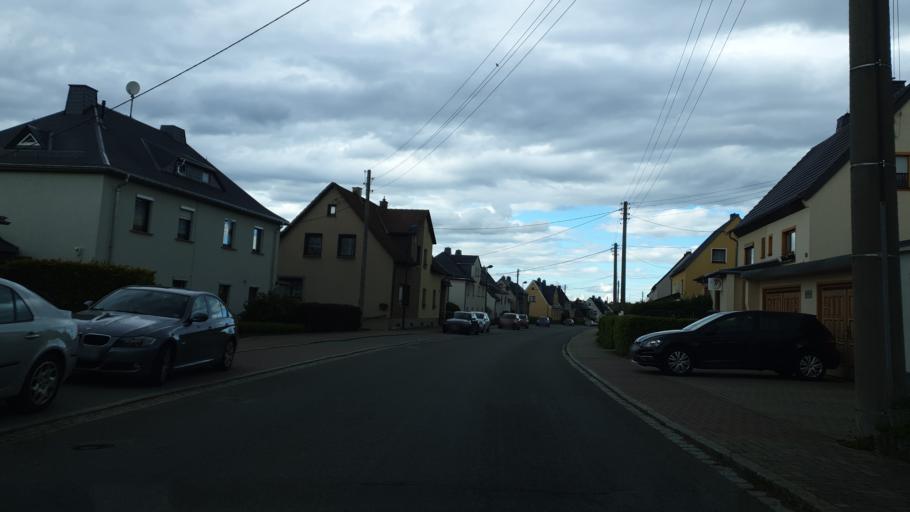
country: DE
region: Saxony
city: Oelsnitz
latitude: 50.7349
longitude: 12.7132
